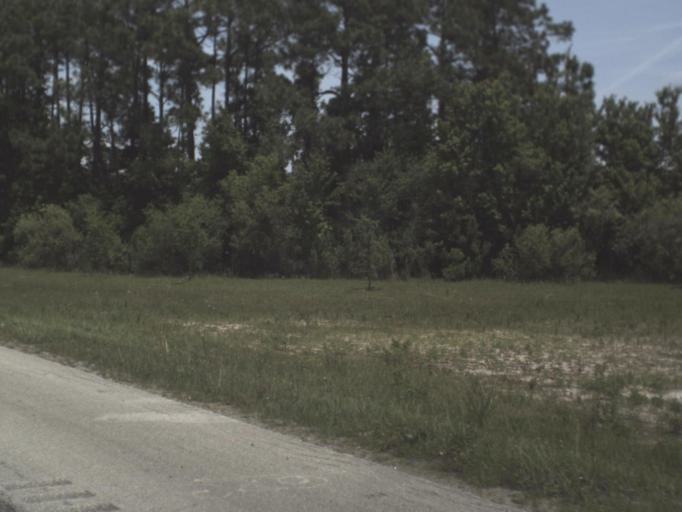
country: US
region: Florida
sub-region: Duval County
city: Jacksonville Beach
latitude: 30.2537
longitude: -81.5163
